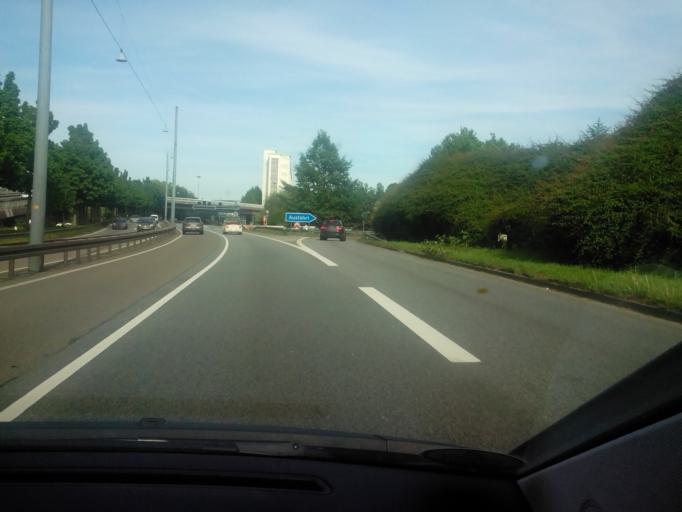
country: DE
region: Saarland
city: Saarbrucken
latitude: 49.2360
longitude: 6.9799
